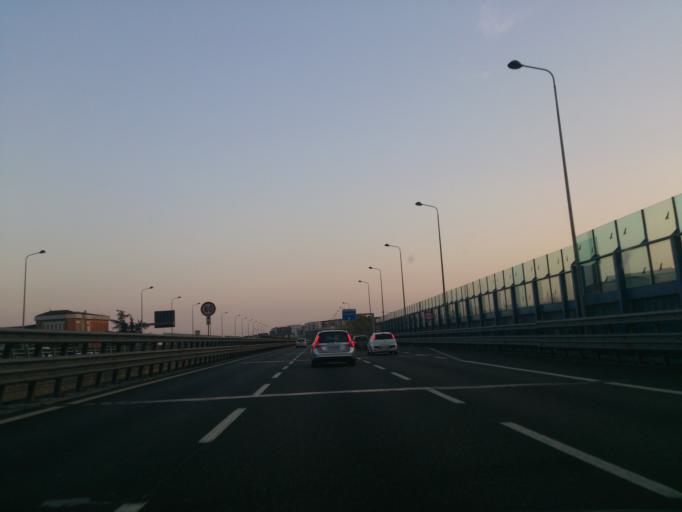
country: IT
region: Lombardy
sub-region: Citta metropolitana di Milano
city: Novegro-Tregarezzo-San Felice
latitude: 45.4884
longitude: 9.2515
